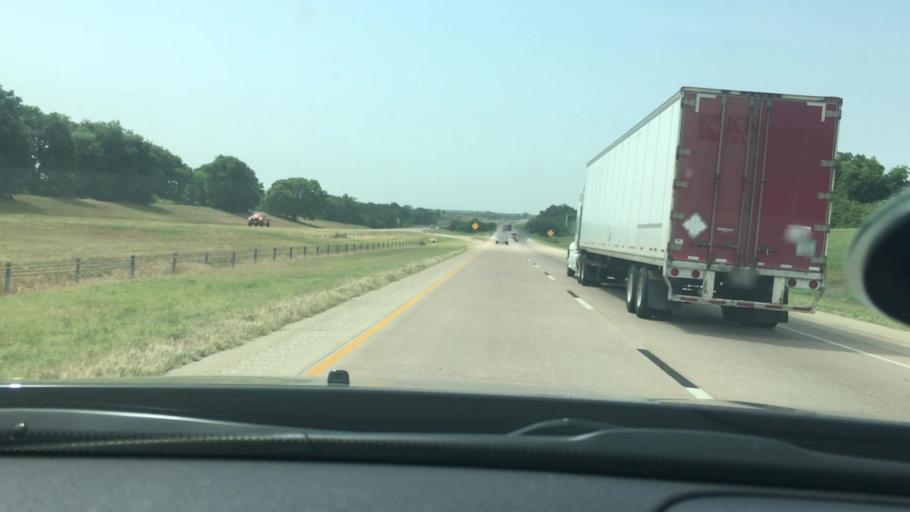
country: US
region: Oklahoma
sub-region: Garvin County
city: Wynnewood
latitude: 34.6700
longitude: -97.2246
